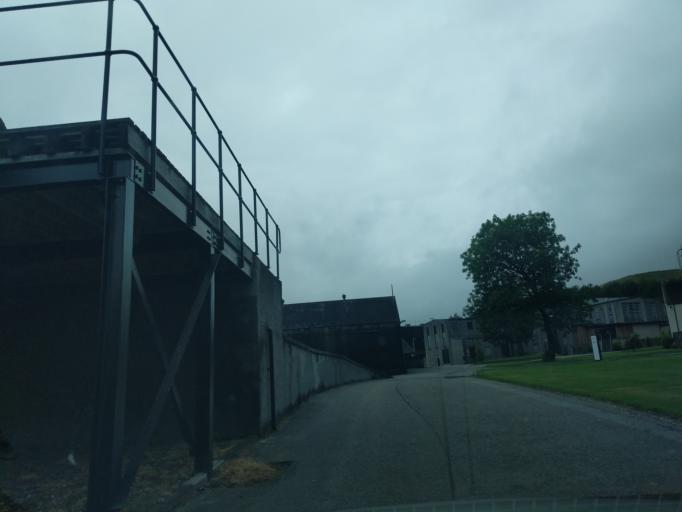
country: GB
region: Scotland
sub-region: Moray
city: Rothes
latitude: 57.4845
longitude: -3.2058
